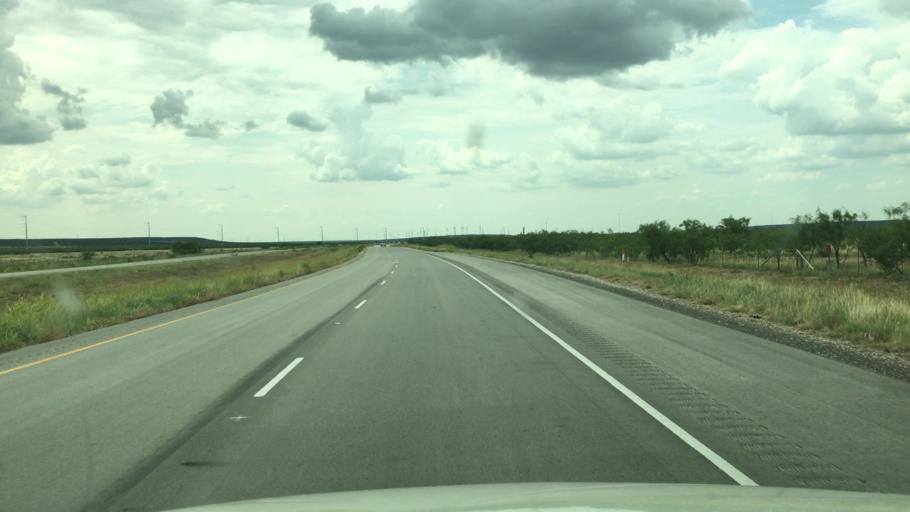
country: US
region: Texas
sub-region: Sterling County
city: Sterling City
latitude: 31.9618
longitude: -101.2159
